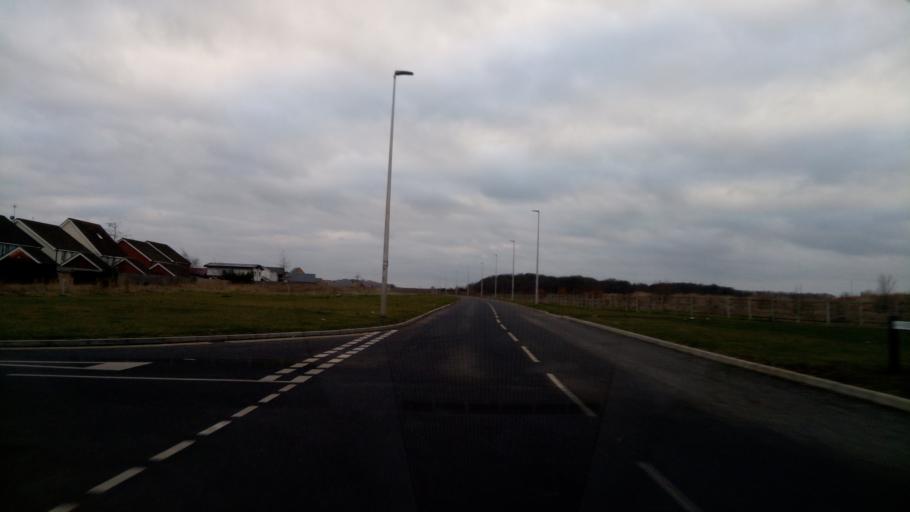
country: GB
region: England
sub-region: Cambridgeshire
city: Yaxley
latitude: 52.5341
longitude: -0.2838
